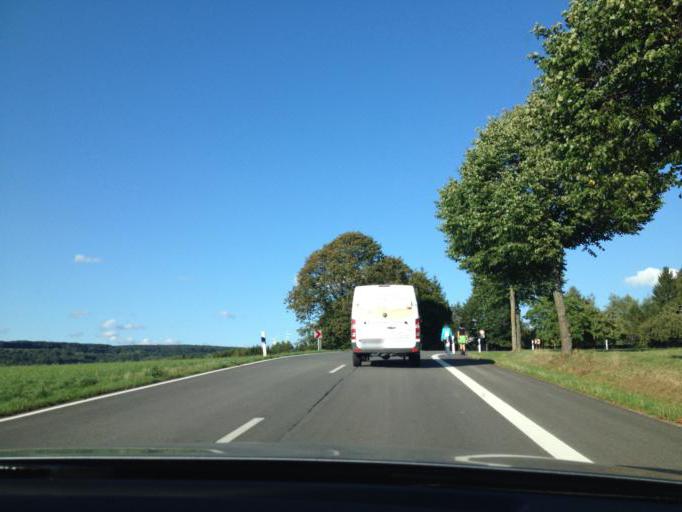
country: DE
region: Saarland
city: Wadern
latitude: 49.4865
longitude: 6.9333
